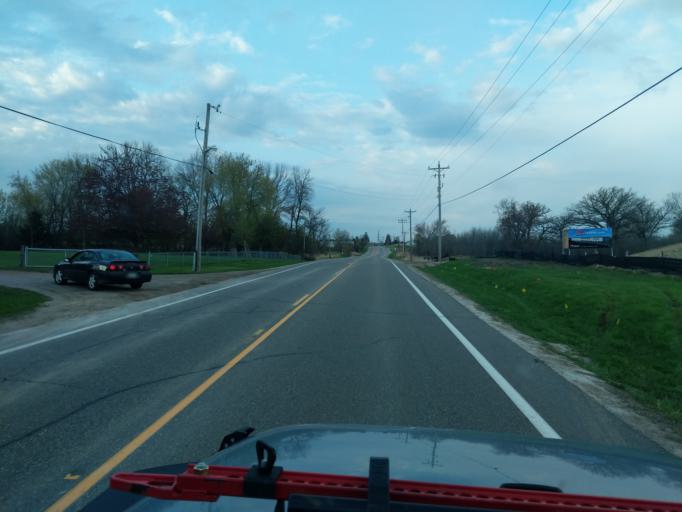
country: US
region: Minnesota
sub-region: Hennepin County
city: Rogers
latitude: 45.1446
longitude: -93.5221
